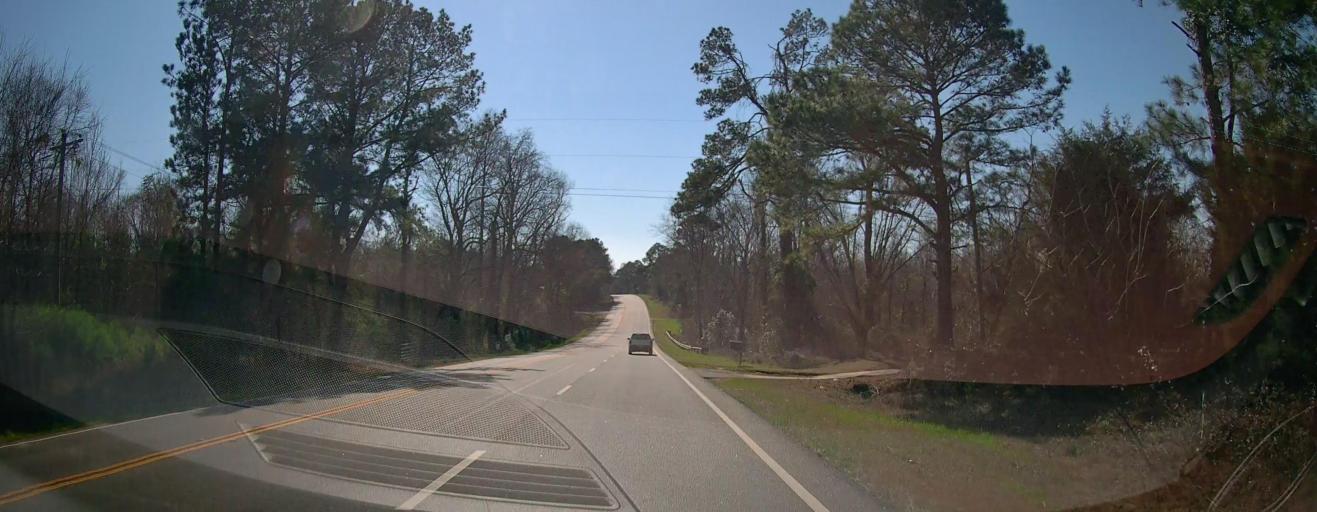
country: US
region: Georgia
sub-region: Macon County
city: Montezuma
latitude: 32.3210
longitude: -83.8879
